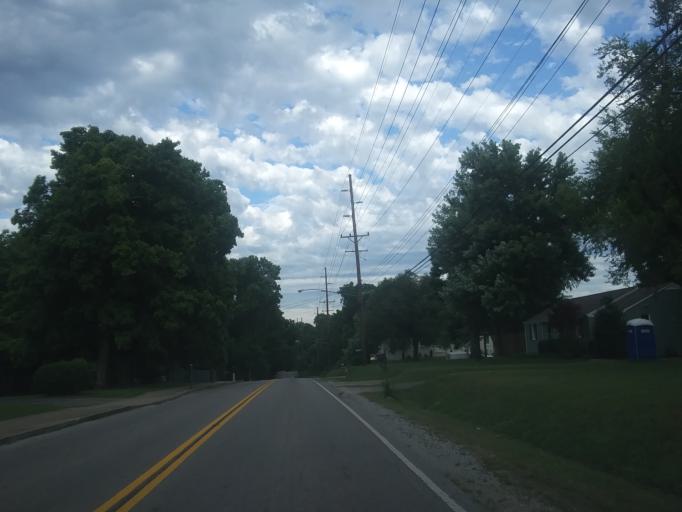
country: US
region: Tennessee
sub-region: Davidson County
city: Oak Hill
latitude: 36.0983
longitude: -86.7263
